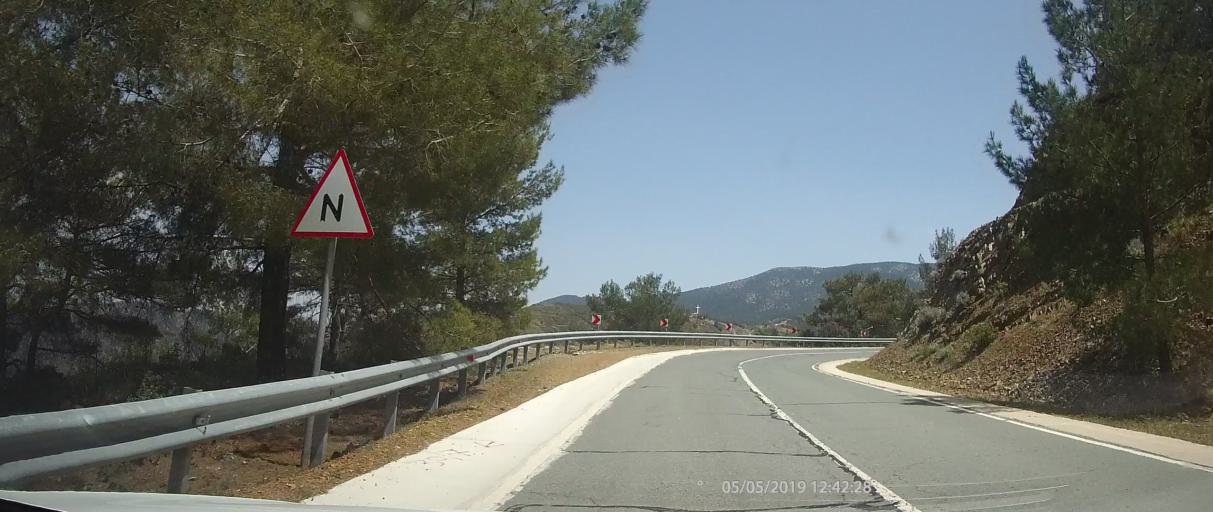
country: CY
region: Lefkosia
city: Kakopetria
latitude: 34.9738
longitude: 32.8106
